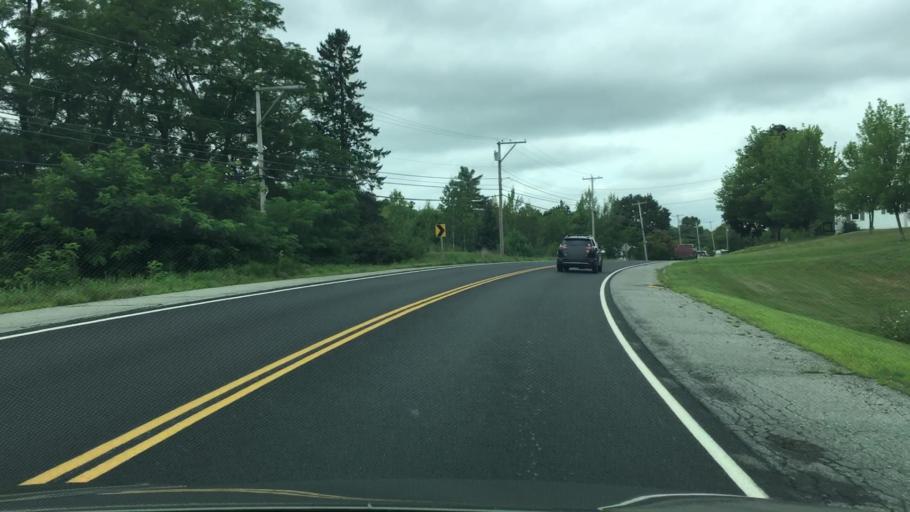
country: US
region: Maine
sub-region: Penobscot County
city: Orrington
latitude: 44.6977
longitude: -68.8195
